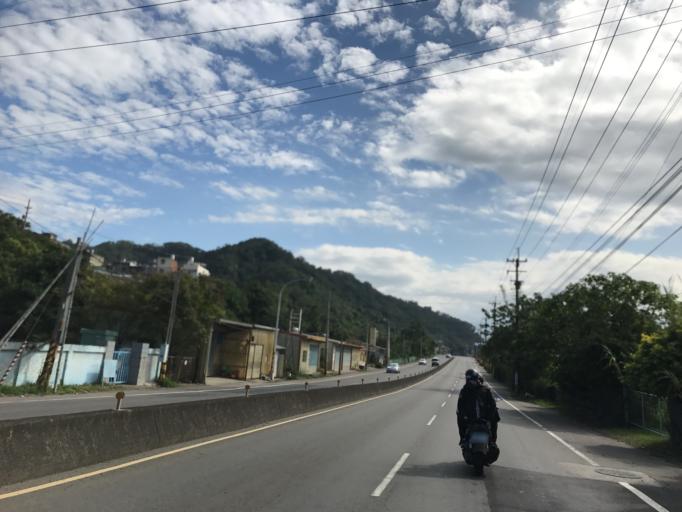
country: TW
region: Taiwan
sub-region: Hsinchu
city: Zhubei
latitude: 24.7454
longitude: 121.1024
